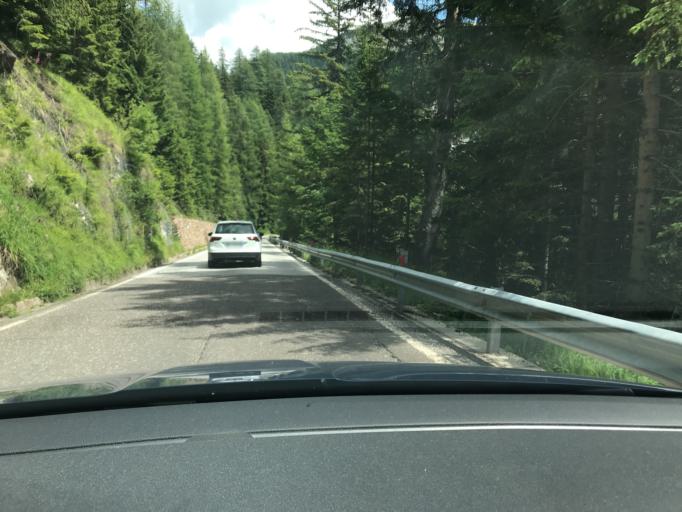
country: IT
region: Trentino-Alto Adige
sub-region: Provincia di Trento
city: Canazei
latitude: 46.4629
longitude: 11.8264
